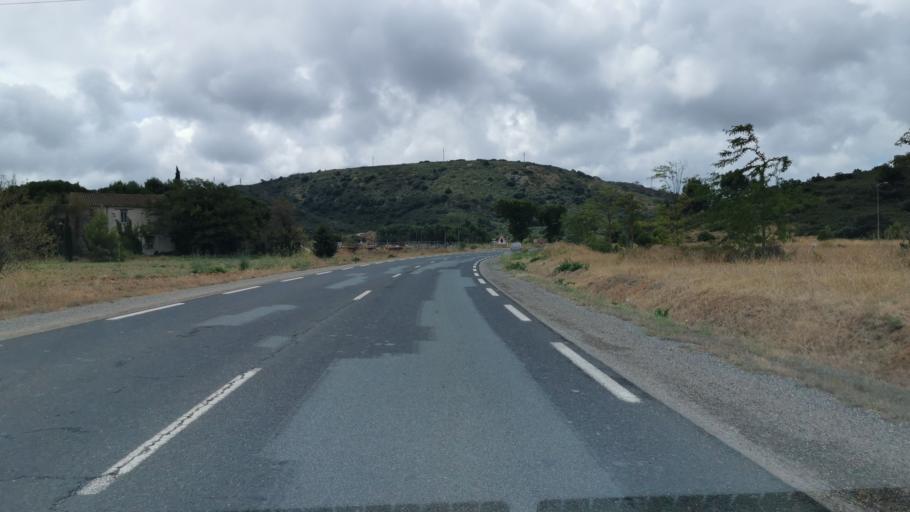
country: FR
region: Languedoc-Roussillon
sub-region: Departement de l'Aude
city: Nevian
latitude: 43.1792
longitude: 2.9338
